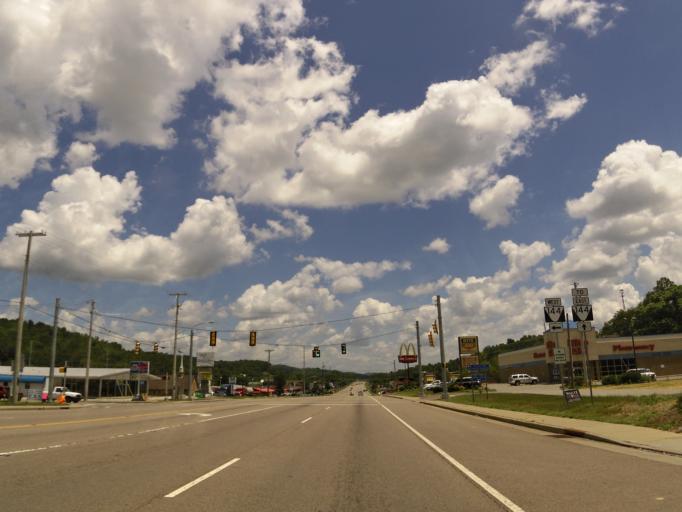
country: US
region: Tennessee
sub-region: Union County
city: Maynardville
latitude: 36.2259
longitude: -83.8451
